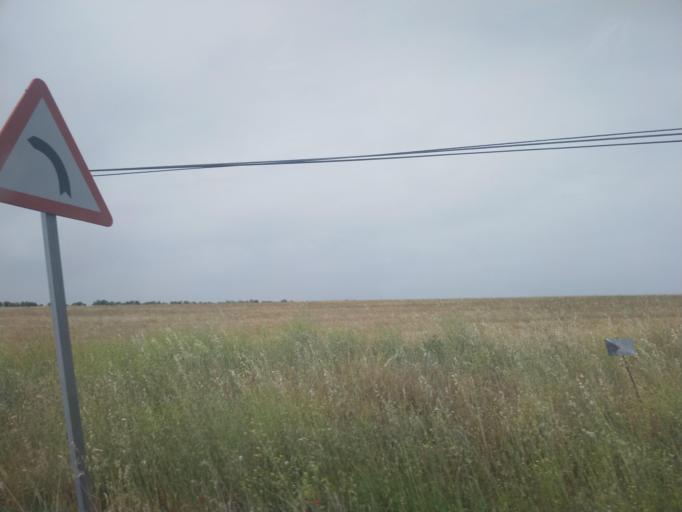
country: ES
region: Castille-La Mancha
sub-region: Province of Toledo
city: Casasbuenas
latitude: 39.7642
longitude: -4.1366
